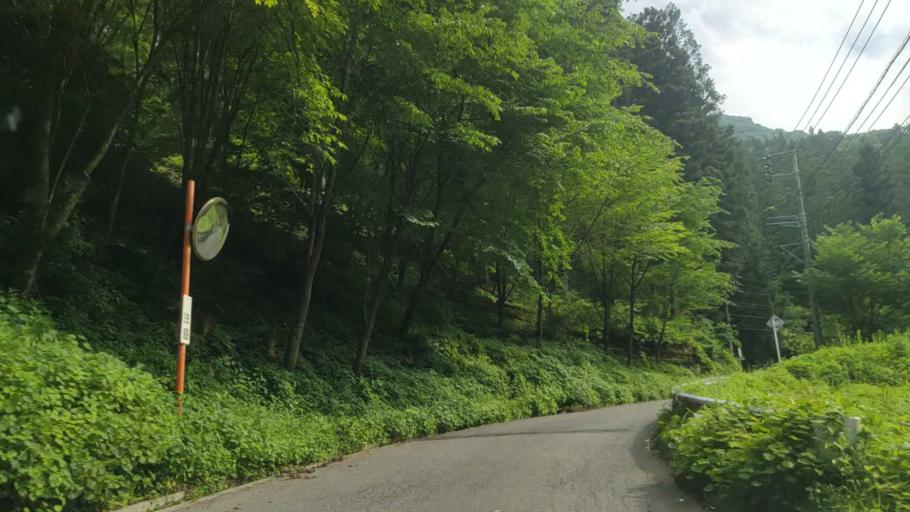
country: JP
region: Gunma
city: Tomioka
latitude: 36.1444
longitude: 138.7325
